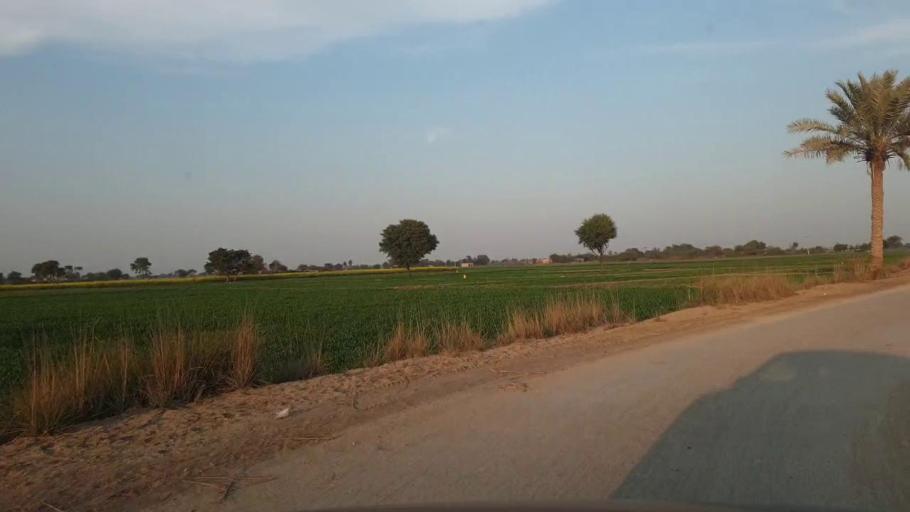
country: PK
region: Sindh
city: Shahpur Chakar
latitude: 26.1817
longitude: 68.6141
